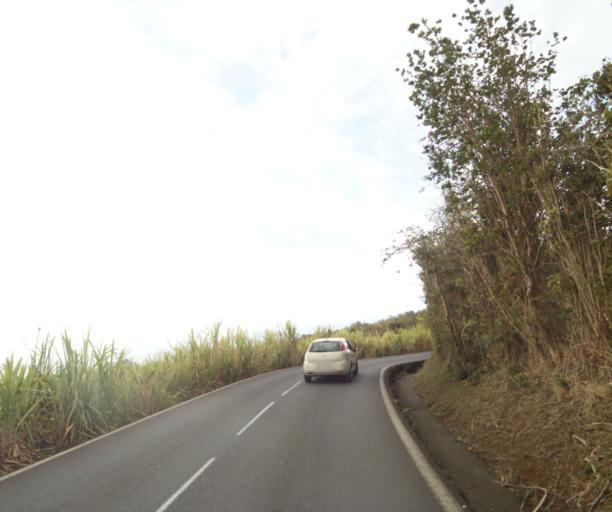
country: RE
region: Reunion
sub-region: Reunion
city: Saint-Paul
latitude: -21.0394
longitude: 55.2906
